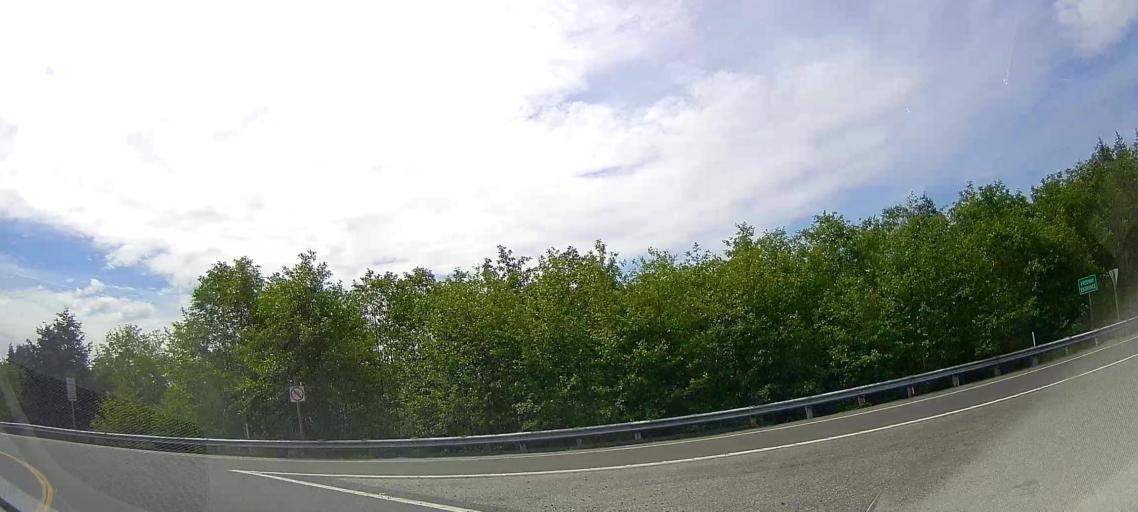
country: US
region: Washington
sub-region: Snohomish County
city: Stanwood
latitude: 48.3094
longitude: -122.3144
